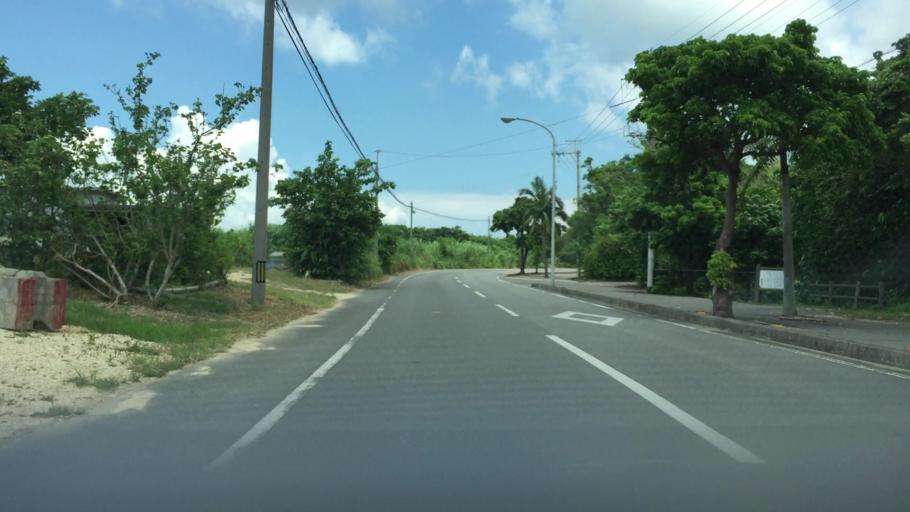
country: JP
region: Okinawa
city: Ishigaki
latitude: 24.3648
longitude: 124.1408
